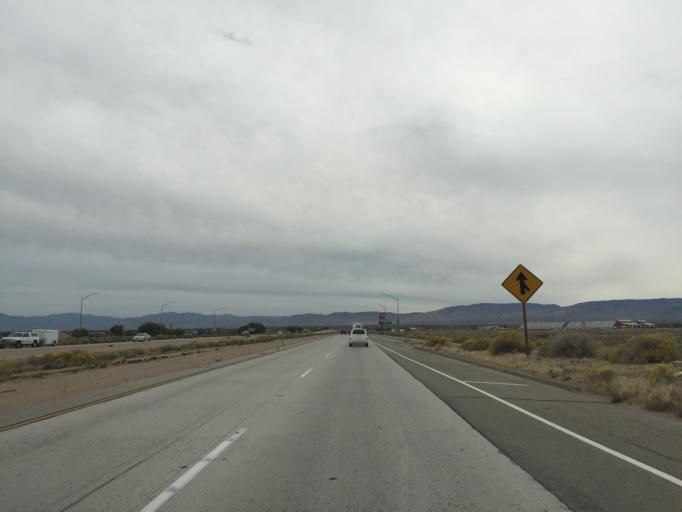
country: US
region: California
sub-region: Los Angeles County
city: Lancaster
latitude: 34.7320
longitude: -118.1705
